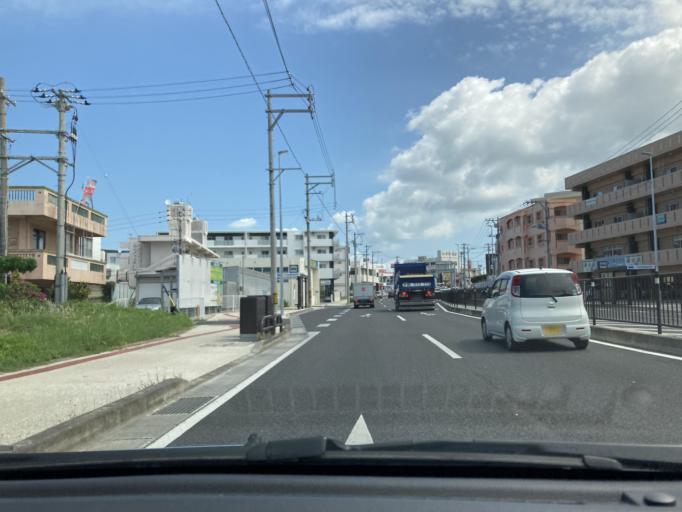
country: JP
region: Okinawa
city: Ginowan
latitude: 26.2568
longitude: 127.7543
